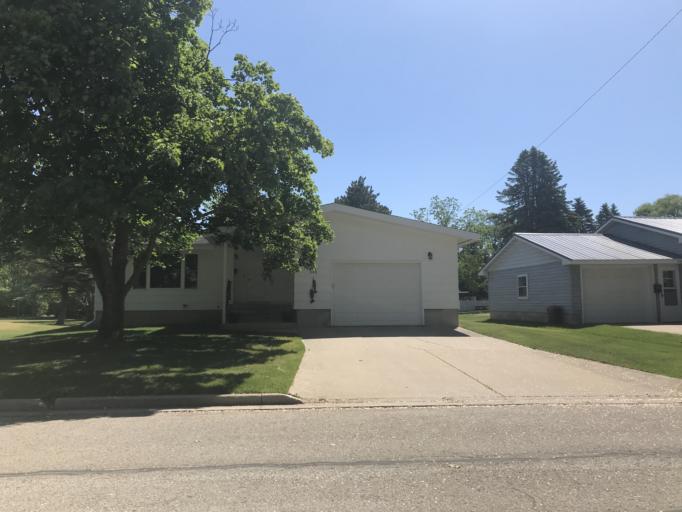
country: US
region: Wisconsin
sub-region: Marinette County
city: Peshtigo
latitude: 45.0587
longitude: -87.7419
